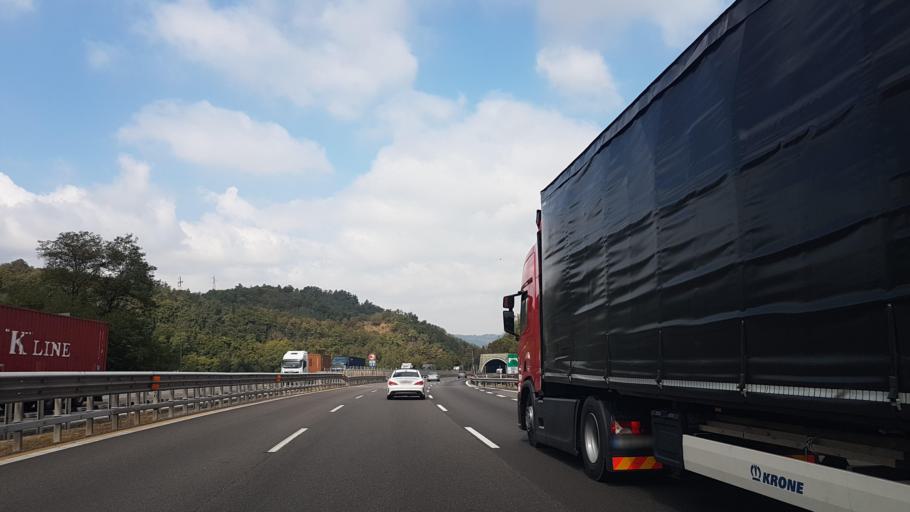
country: IT
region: Piedmont
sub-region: Provincia di Alessandria
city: Belforte Monferrato
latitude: 44.6143
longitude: 8.6569
